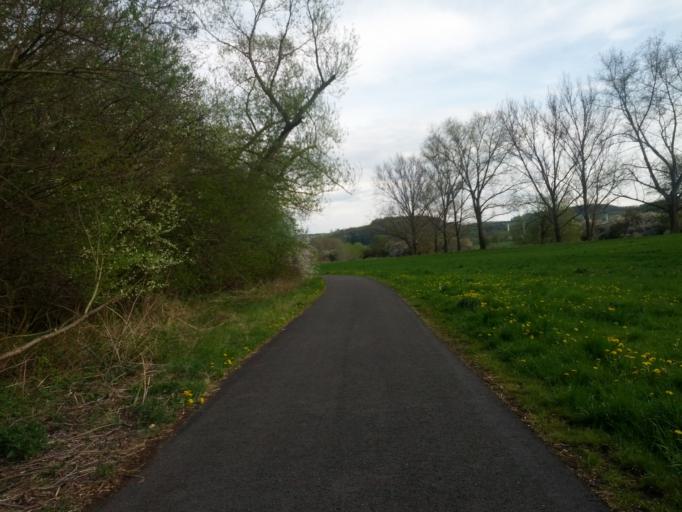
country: DE
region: Thuringia
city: Creuzburg
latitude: 51.0332
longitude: 10.2292
